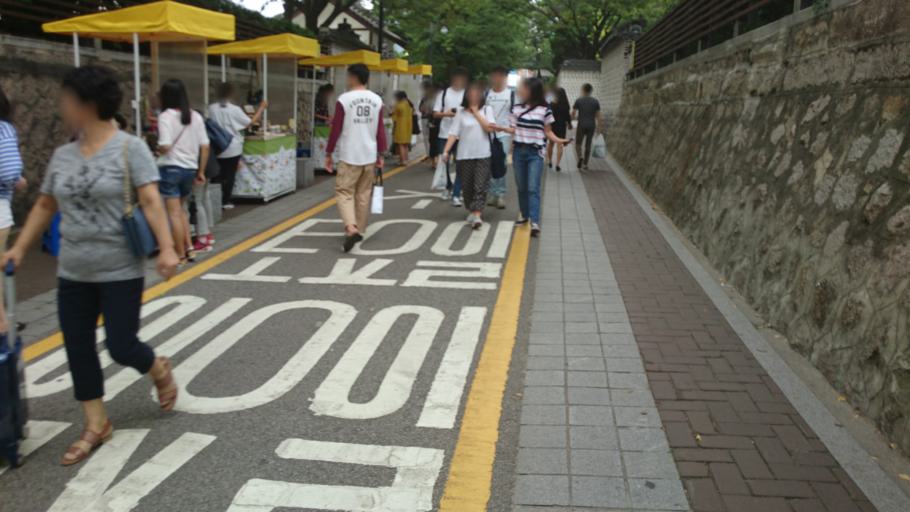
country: KR
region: Seoul
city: Seoul
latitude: 37.5775
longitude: 126.9825
